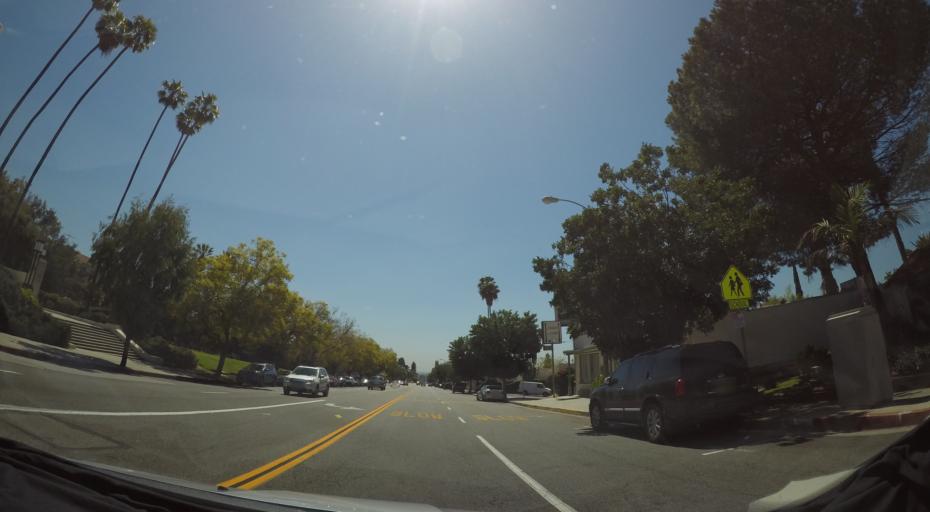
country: US
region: California
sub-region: Los Angeles County
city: Altadena
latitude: 34.1836
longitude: -118.1316
